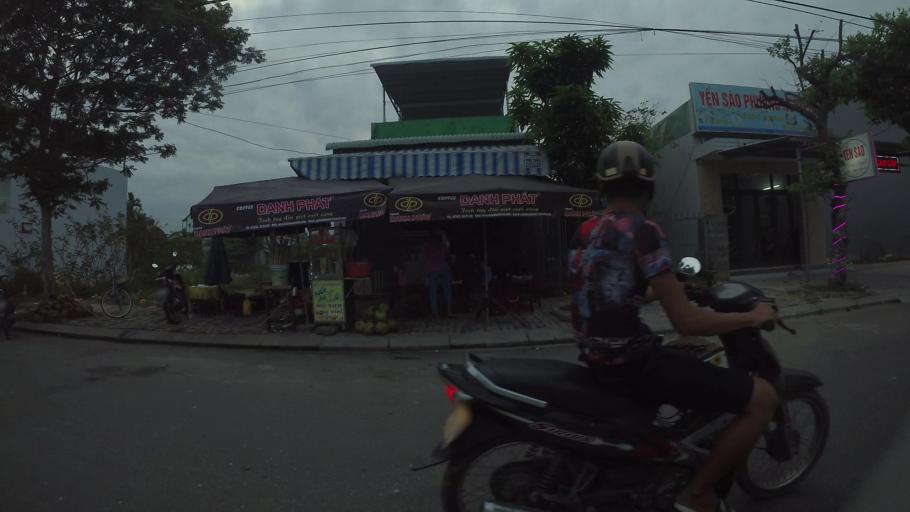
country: VN
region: Da Nang
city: Lien Chieu
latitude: 16.0704
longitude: 108.1060
